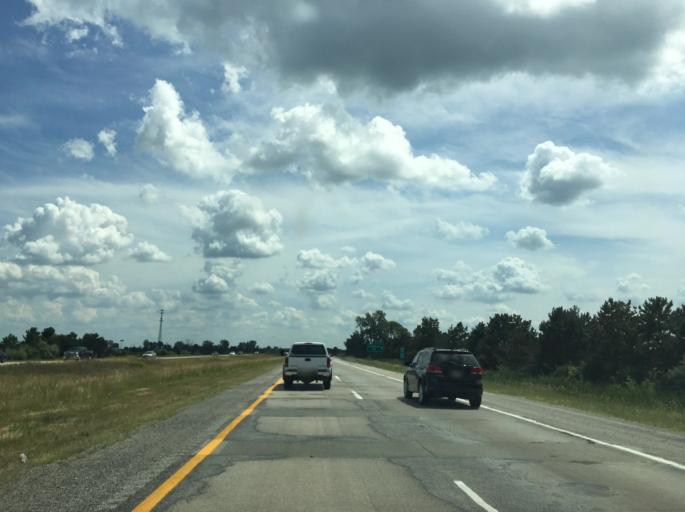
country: US
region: Michigan
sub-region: Bay County
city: Pinconning
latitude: 43.7481
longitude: -84.0173
